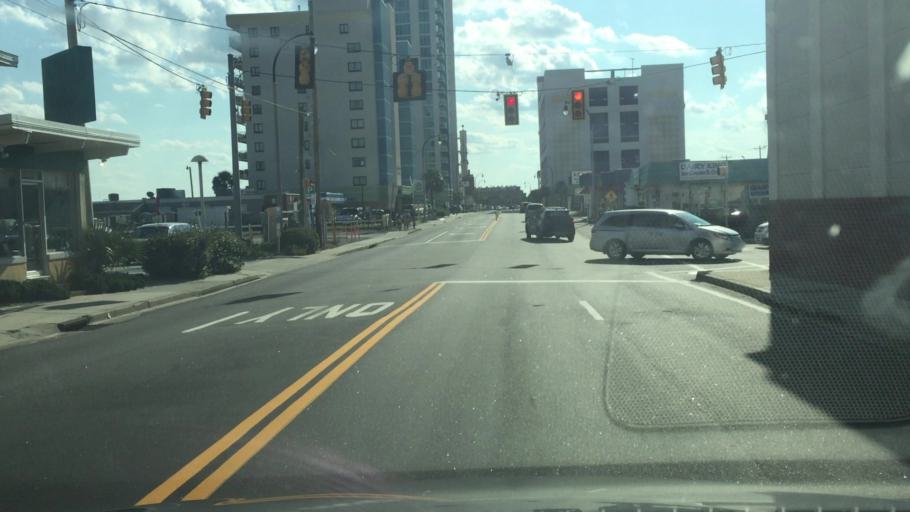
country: US
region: South Carolina
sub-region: Horry County
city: North Myrtle Beach
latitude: 33.8280
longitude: -78.6427
